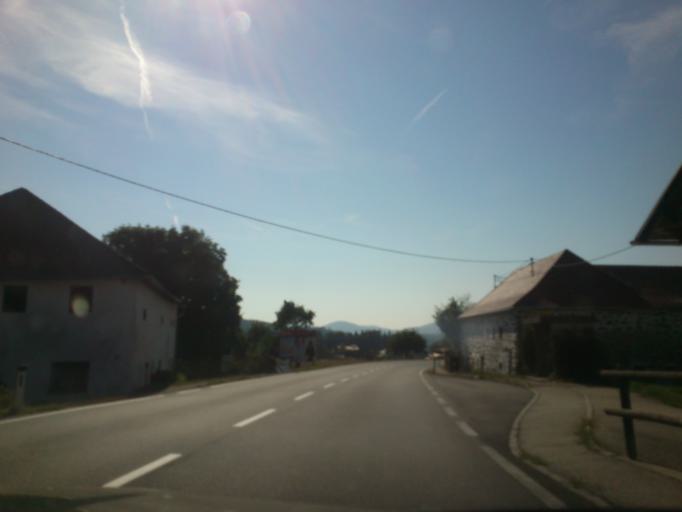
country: AT
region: Upper Austria
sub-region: Politischer Bezirk Freistadt
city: Freistadt
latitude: 48.5338
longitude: 14.5023
